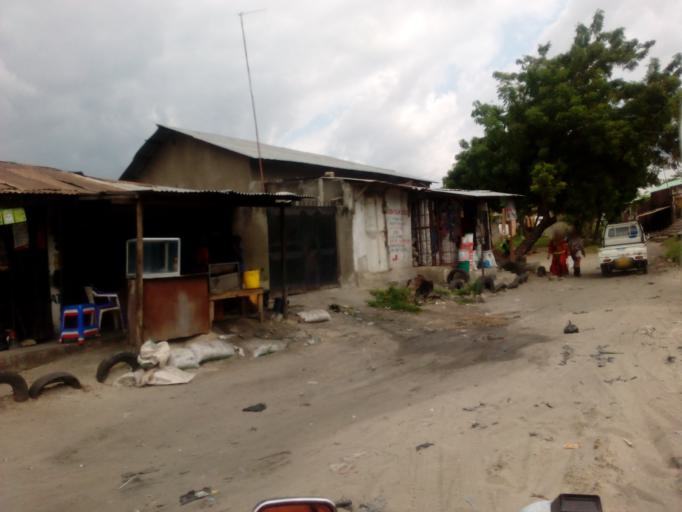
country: TZ
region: Dar es Salaam
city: Dar es Salaam
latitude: -6.8522
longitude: 39.2543
